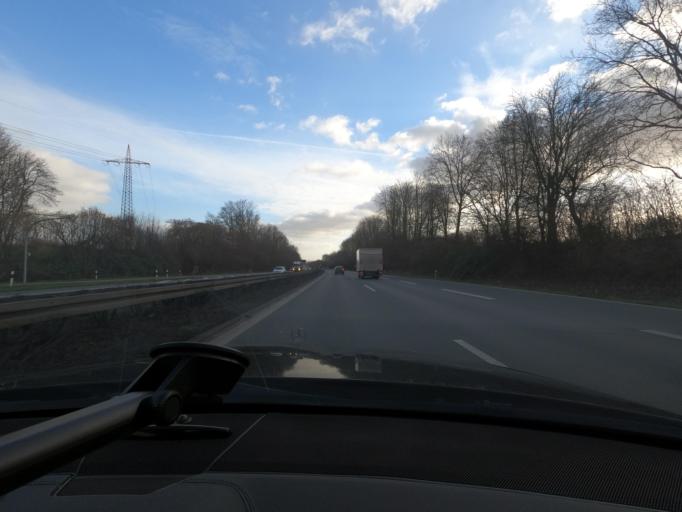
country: DE
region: North Rhine-Westphalia
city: Lunen
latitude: 51.5642
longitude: 7.5046
